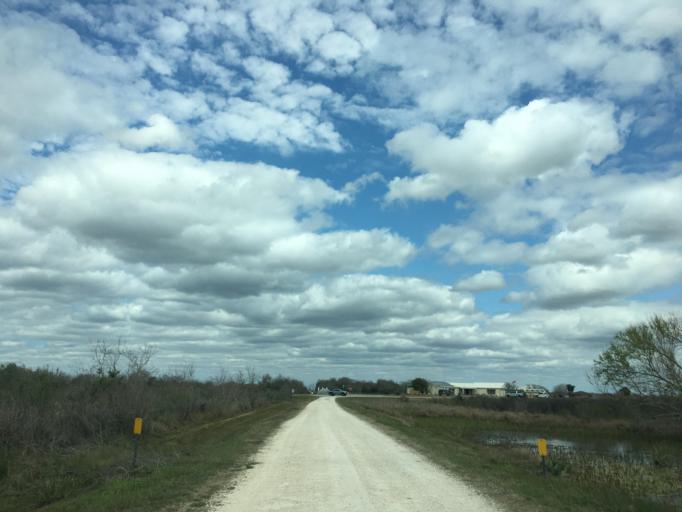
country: US
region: Texas
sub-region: Brazoria County
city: Oyster Creek
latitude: 29.0580
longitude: -95.2687
